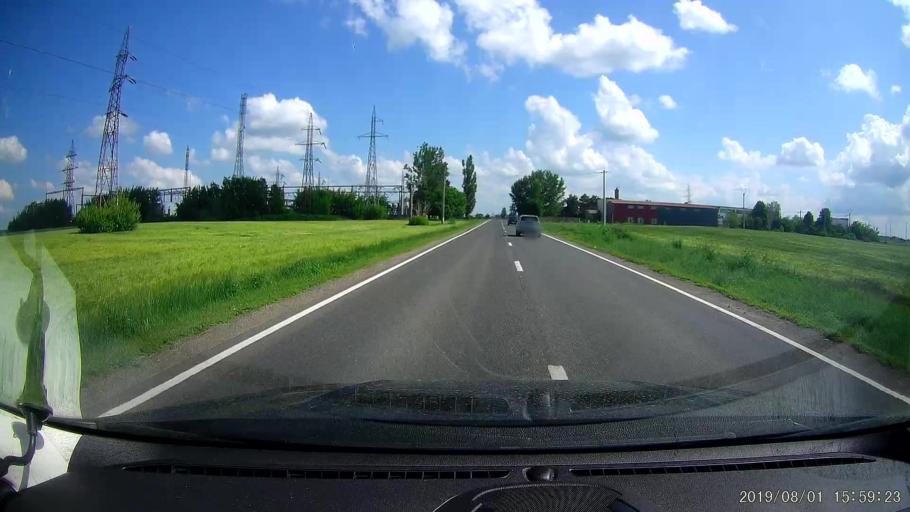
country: RO
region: Ialomita
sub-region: Comuna Slobozia
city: Slobozia
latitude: 44.5496
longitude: 27.3831
